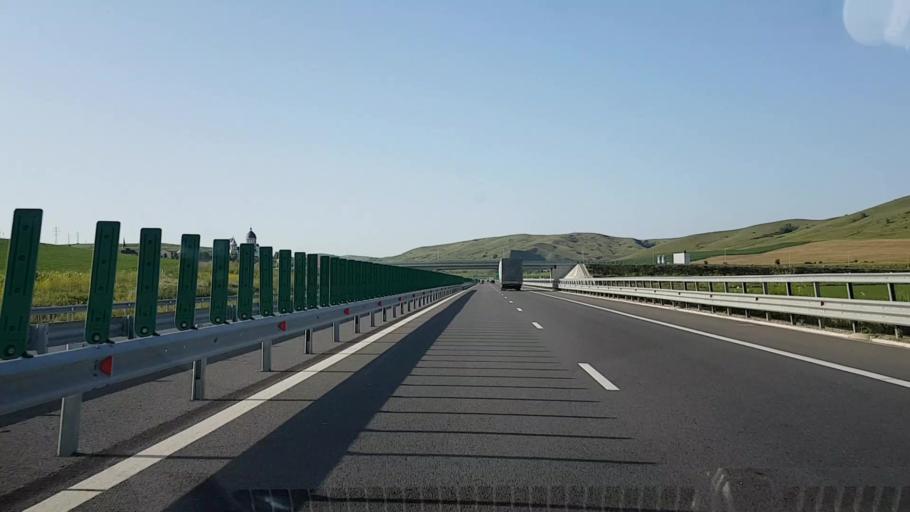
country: RO
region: Alba
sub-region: Comuna Unirea
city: Unirea
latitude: 46.4320
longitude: 23.7975
